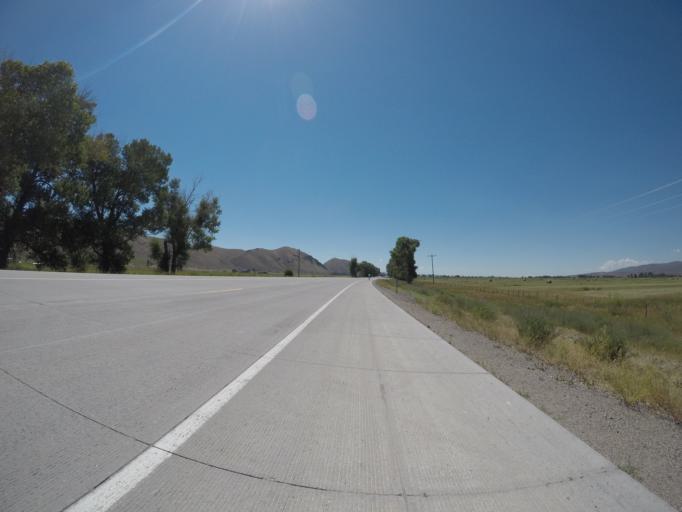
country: US
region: Idaho
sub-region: Bear Lake County
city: Montpelier
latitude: 42.1158
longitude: -110.9587
